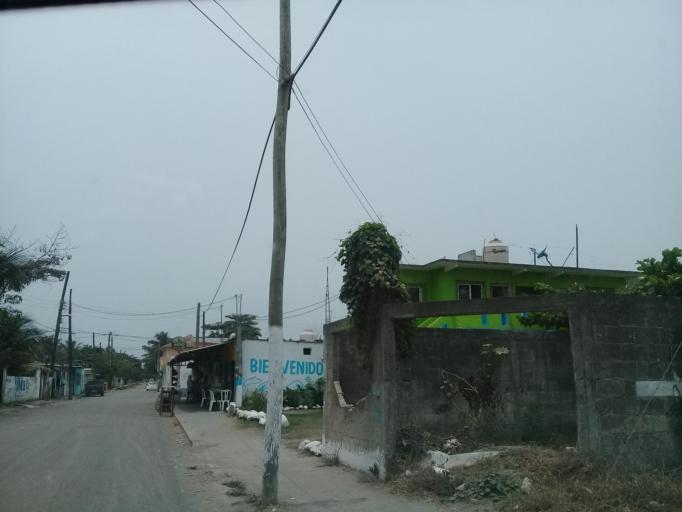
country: MX
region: Veracruz
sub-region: Veracruz
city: Las Amapolas
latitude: 19.1407
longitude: -96.2018
